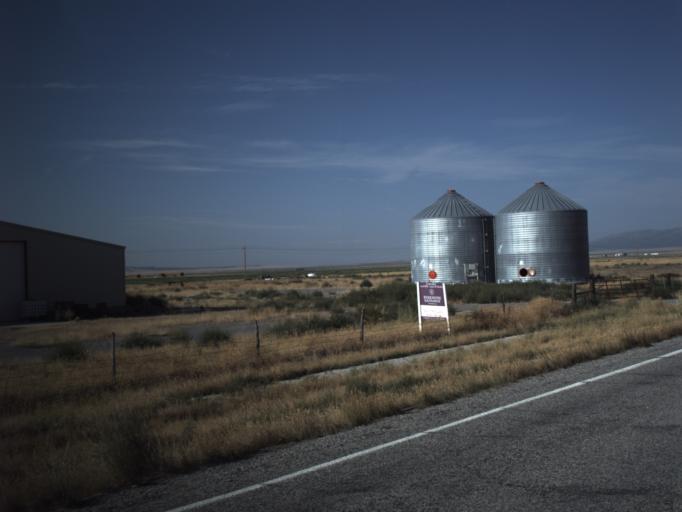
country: US
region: Idaho
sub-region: Oneida County
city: Malad City
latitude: 41.9666
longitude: -112.9031
